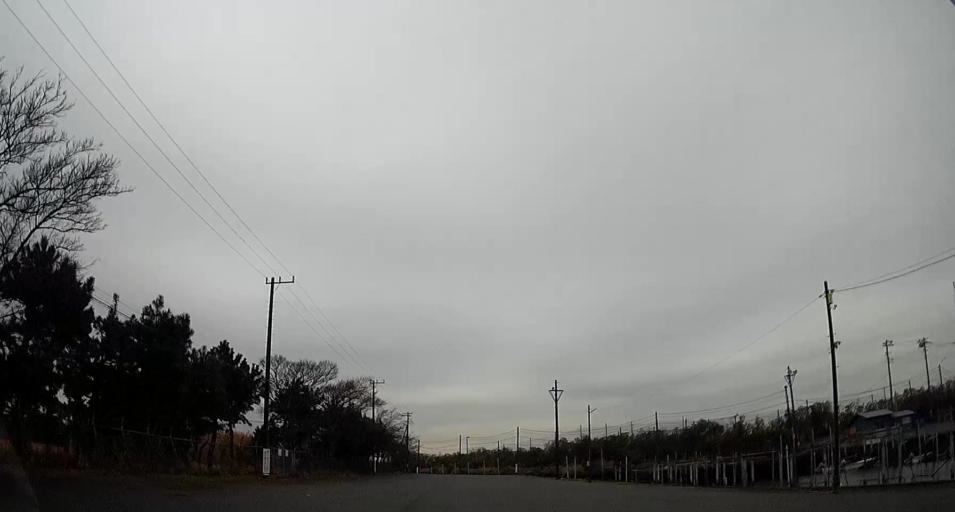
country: JP
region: Chiba
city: Kisarazu
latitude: 35.4050
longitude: 139.9038
